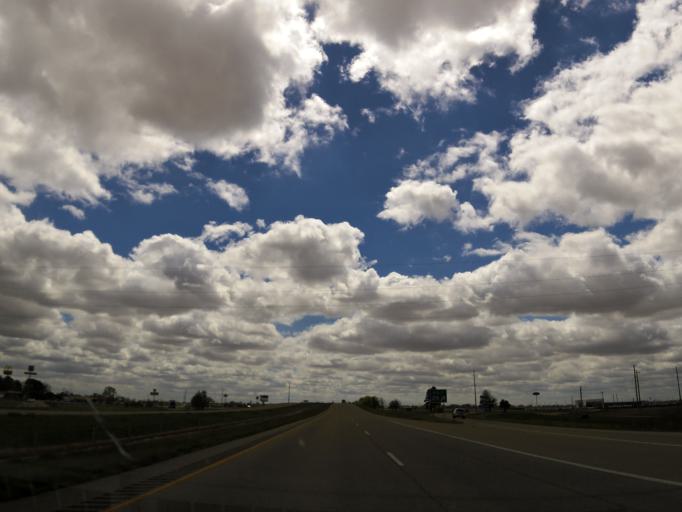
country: US
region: Arkansas
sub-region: Poinsett County
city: Trumann
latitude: 35.6824
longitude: -90.5529
